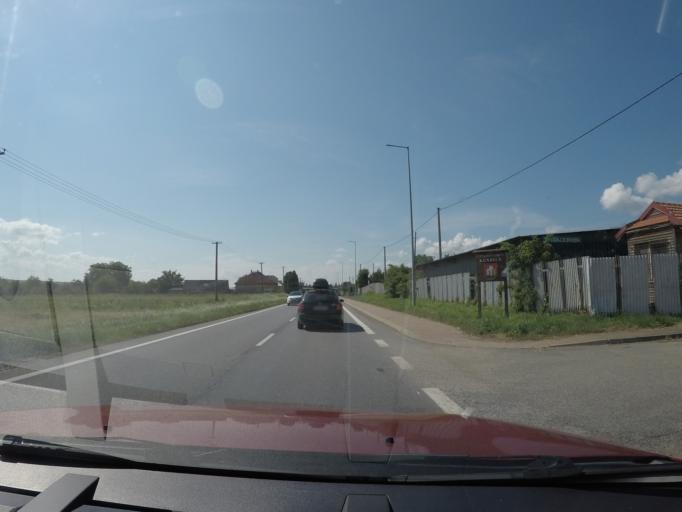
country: SK
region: Presovsky
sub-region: Okres Presov
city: Presov
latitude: 48.9330
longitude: 21.2406
